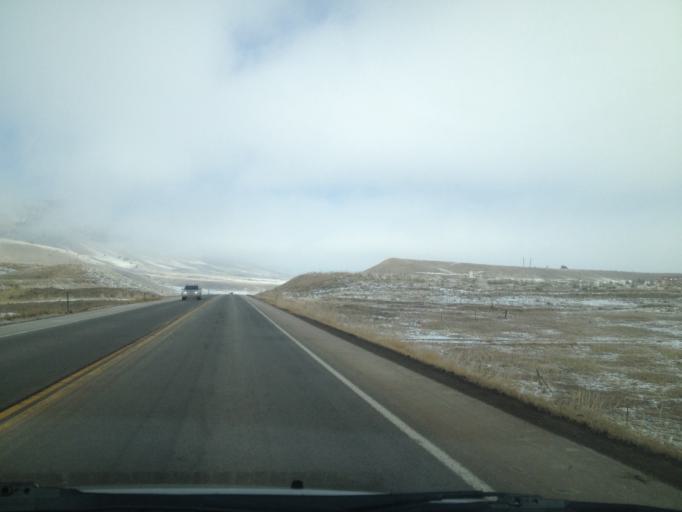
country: US
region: Colorado
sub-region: Boulder County
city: Boulder
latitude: 40.0697
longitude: -105.2835
